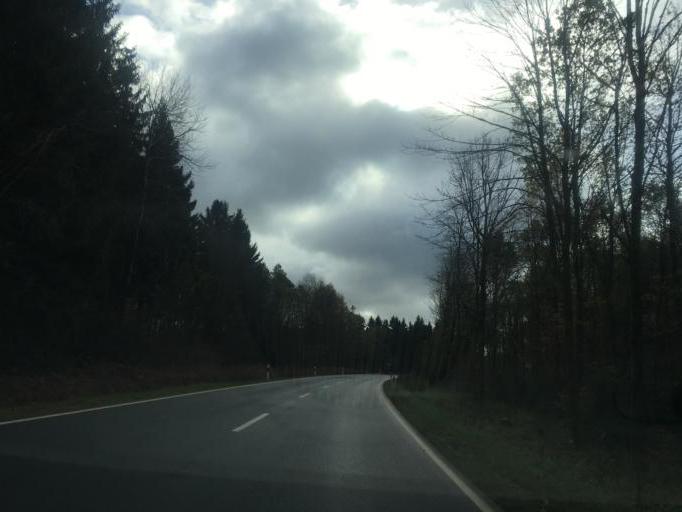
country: DE
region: Lower Saxony
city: Bevern
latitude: 51.7685
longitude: 9.5296
